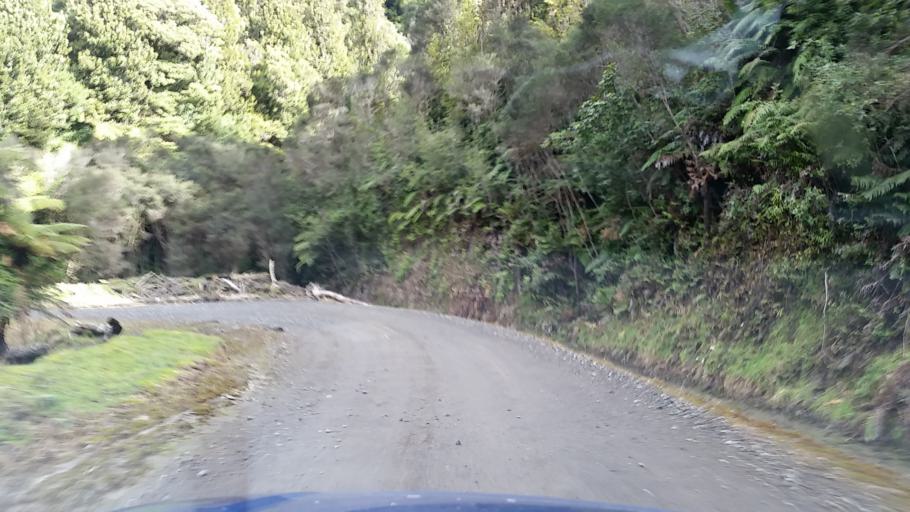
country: NZ
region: Taranaki
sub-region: South Taranaki District
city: Eltham
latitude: -39.2798
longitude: 174.7561
